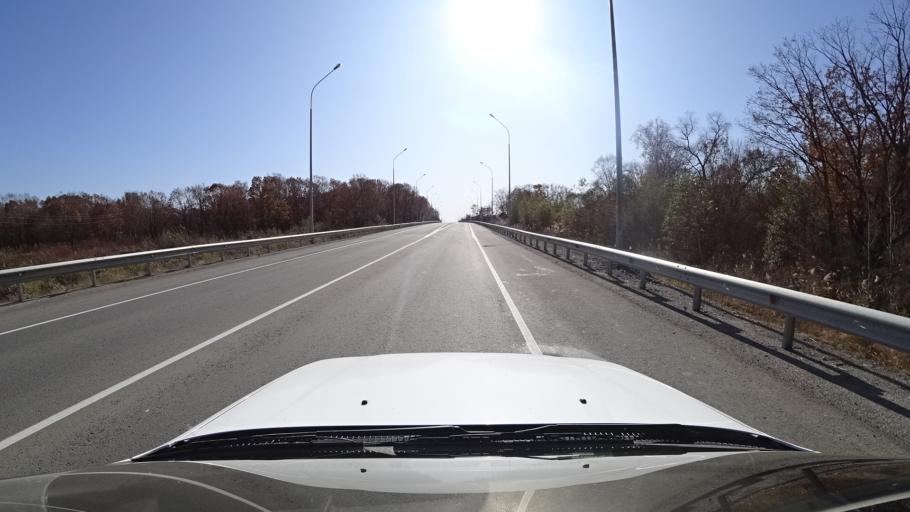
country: RU
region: Primorskiy
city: Dal'nerechensk
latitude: 45.8848
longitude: 133.7304
